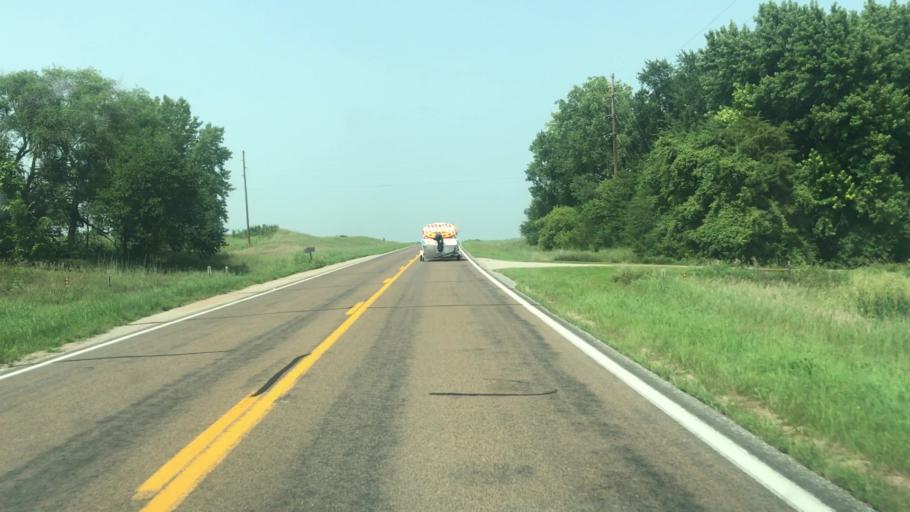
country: US
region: Nebraska
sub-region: Sherman County
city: Loup City
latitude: 41.2487
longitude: -98.9390
